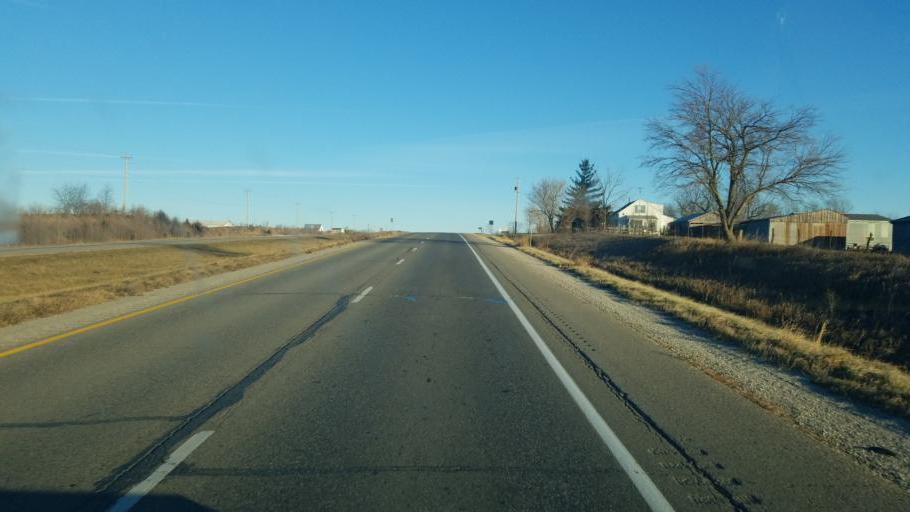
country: US
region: Iowa
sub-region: Mahaska County
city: Oskaloosa
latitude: 41.2287
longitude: -92.6405
